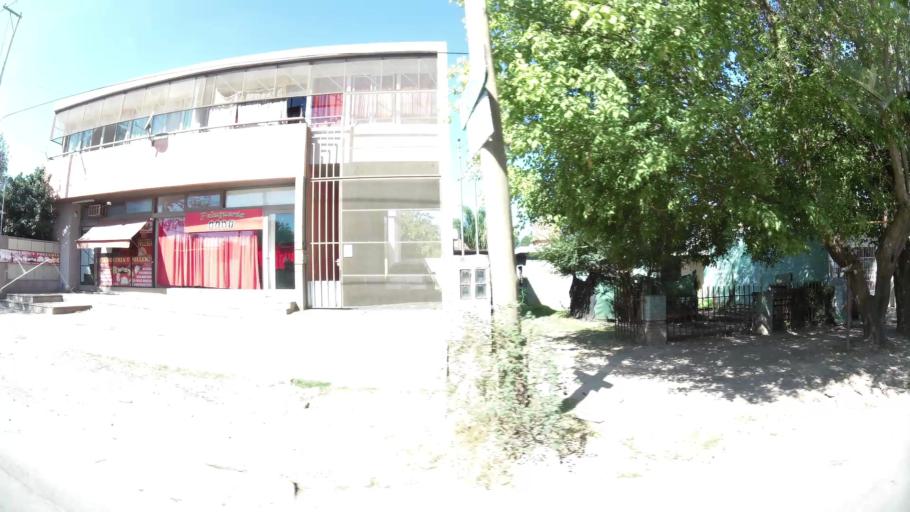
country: AR
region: Cordoba
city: Saldan
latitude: -31.3250
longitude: -64.2886
